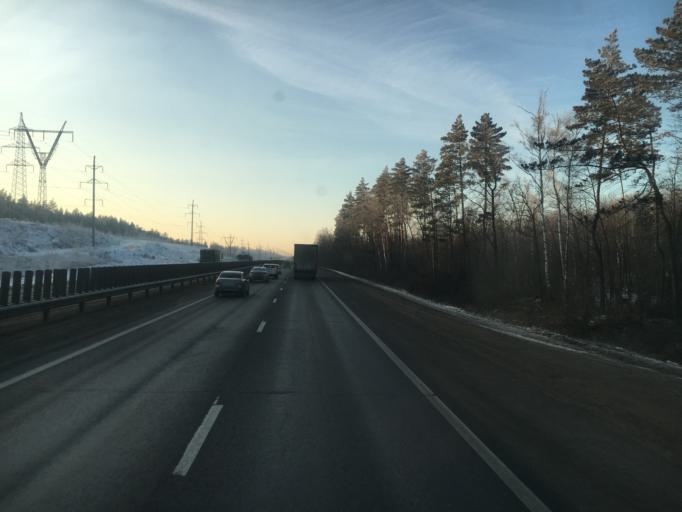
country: RU
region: Samara
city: Pribrezhnyy
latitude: 53.5143
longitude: 49.8944
